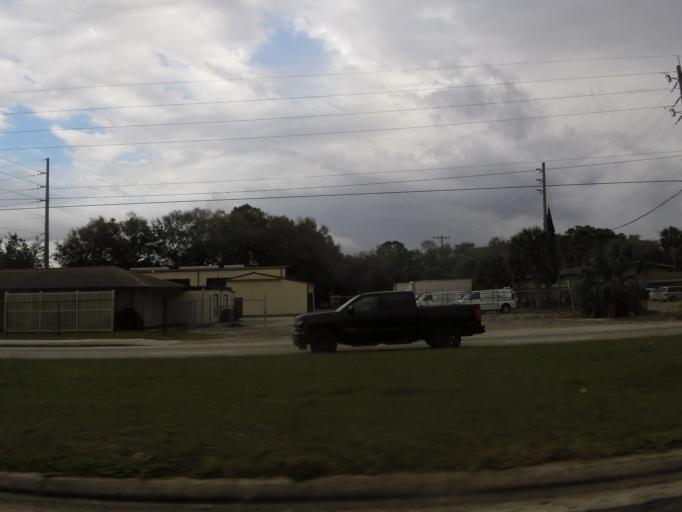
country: US
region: Florida
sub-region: Duval County
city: Jacksonville
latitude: 30.3273
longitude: -81.5922
